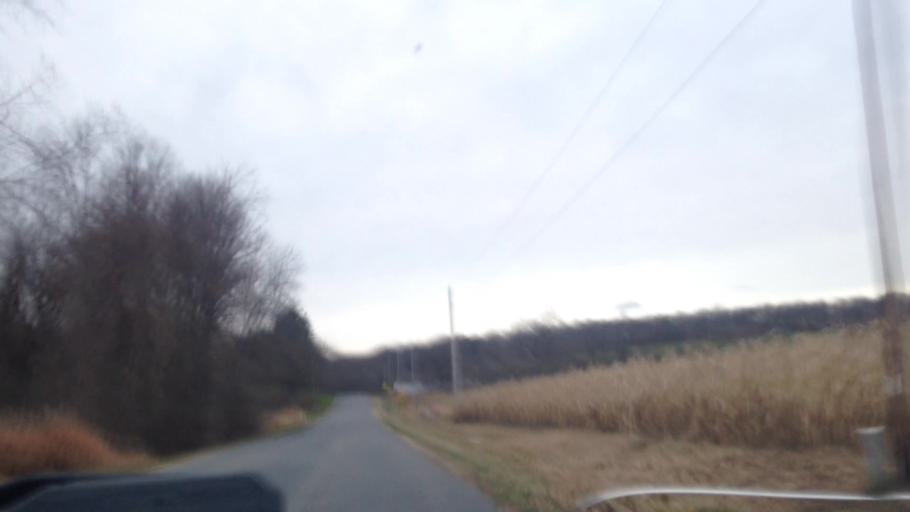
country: US
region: Wisconsin
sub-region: Dodge County
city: Theresa
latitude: 43.4862
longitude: -88.4929
